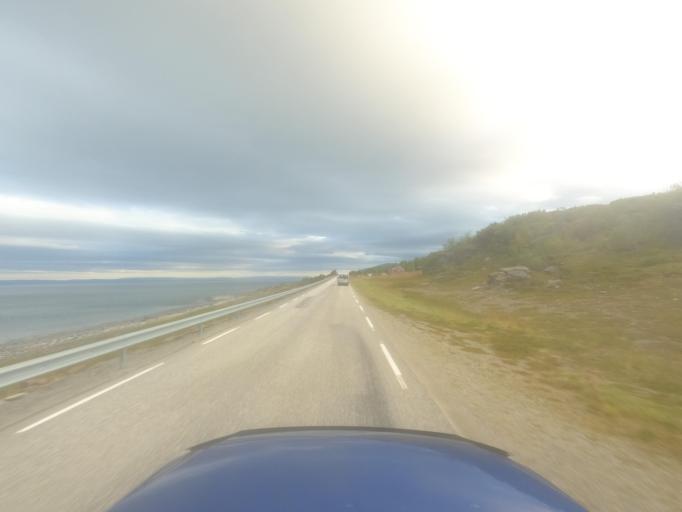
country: NO
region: Finnmark Fylke
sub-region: Porsanger
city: Lakselv
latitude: 70.5843
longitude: 25.2471
